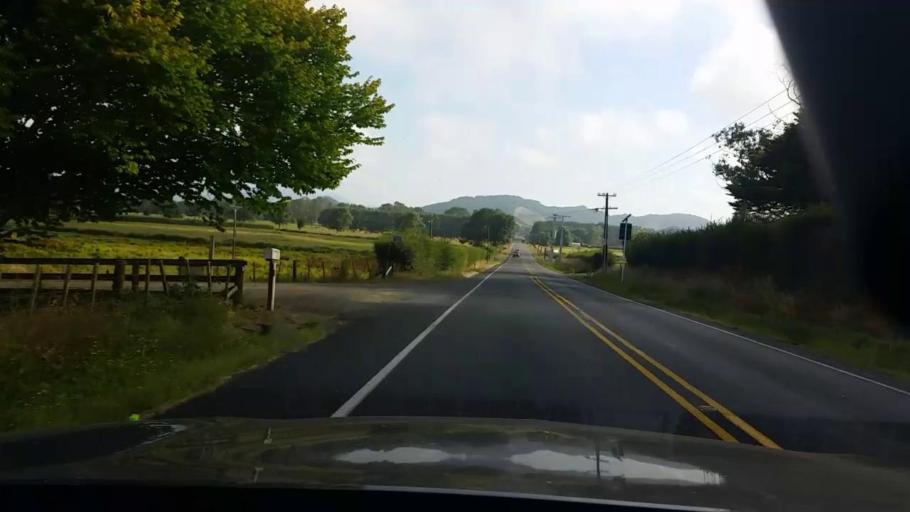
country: NZ
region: Waikato
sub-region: Hamilton City
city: Hamilton
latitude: -37.6107
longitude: 175.3465
